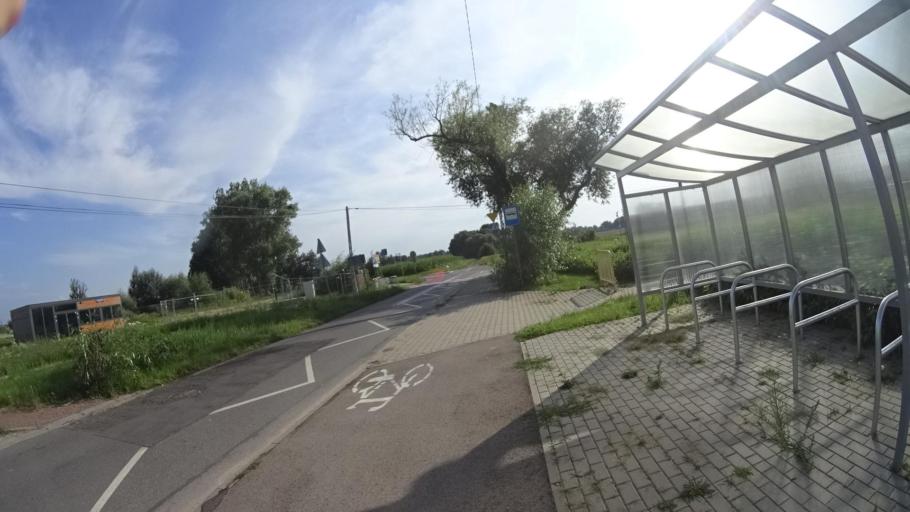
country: PL
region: Masovian Voivodeship
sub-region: Powiat pruszkowski
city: Nadarzyn
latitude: 52.0622
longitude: 20.7868
